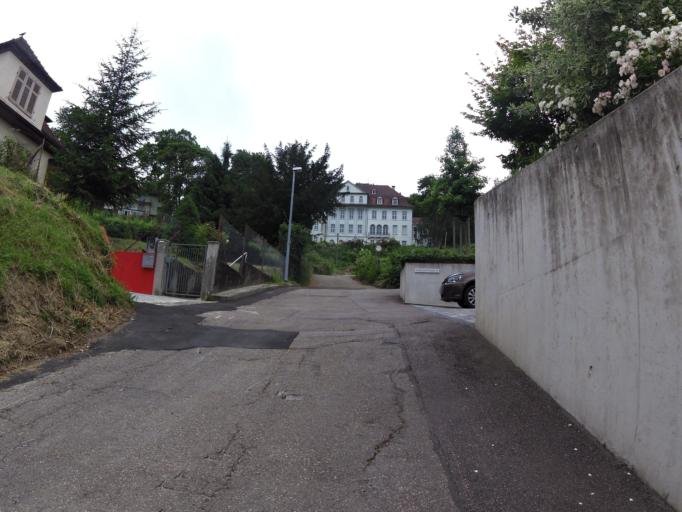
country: DE
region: Baden-Wuerttemberg
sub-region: Freiburg Region
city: Lahr
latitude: 48.3417
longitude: 7.8890
